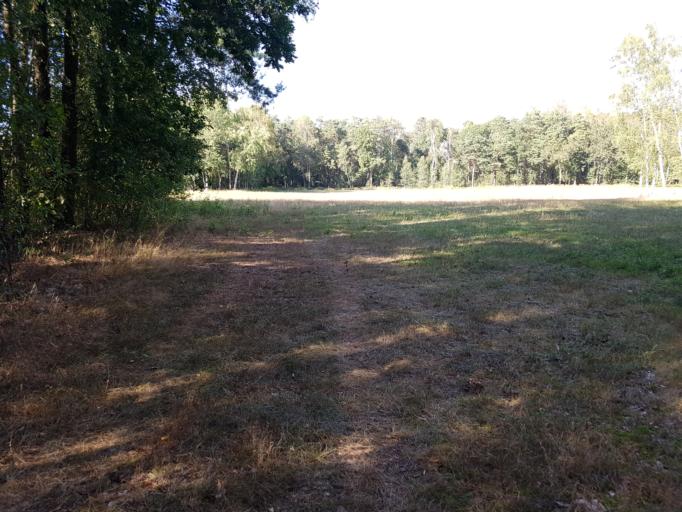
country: DE
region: Brandenburg
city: Doberlug-Kirchhain
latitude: 51.6311
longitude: 13.5952
